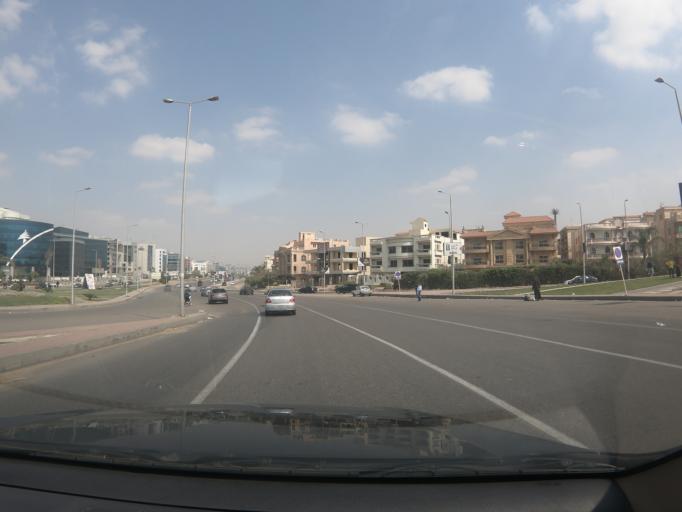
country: EG
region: Muhafazat al Qahirah
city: Cairo
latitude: 30.0159
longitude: 31.4165
